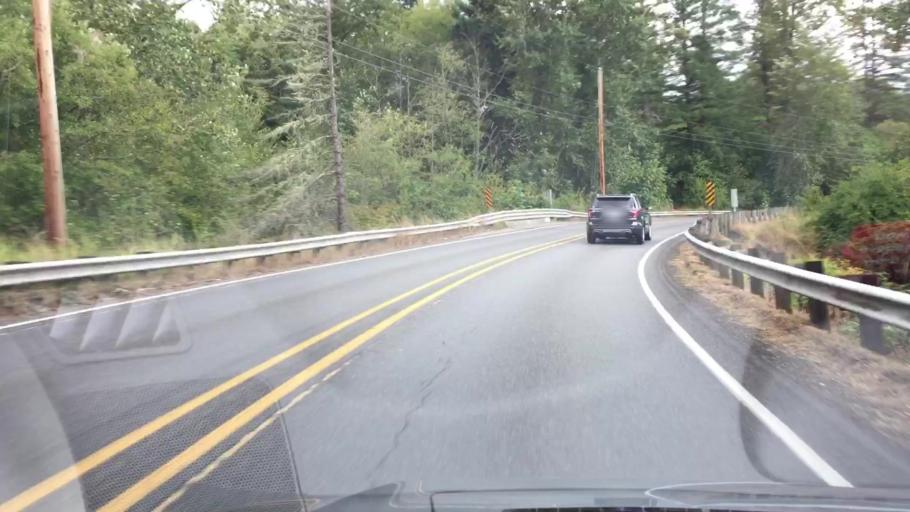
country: US
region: Washington
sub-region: Pierce County
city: Eatonville
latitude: 46.8484
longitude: -122.2518
